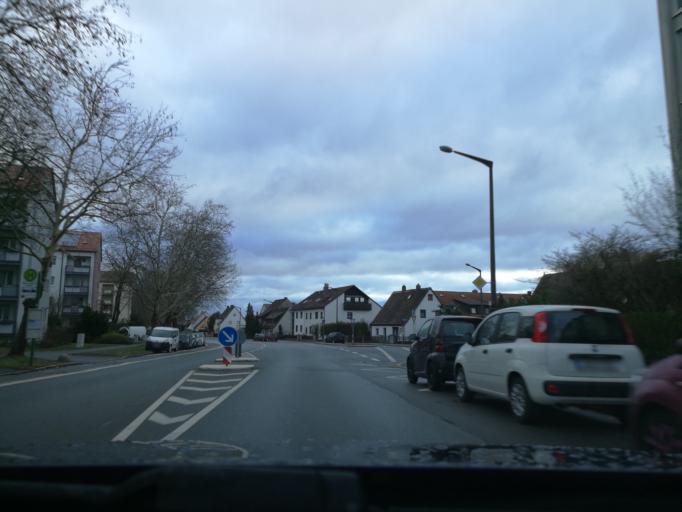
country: DE
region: Bavaria
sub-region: Regierungsbezirk Mittelfranken
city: Furth
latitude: 49.4781
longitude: 10.9589
